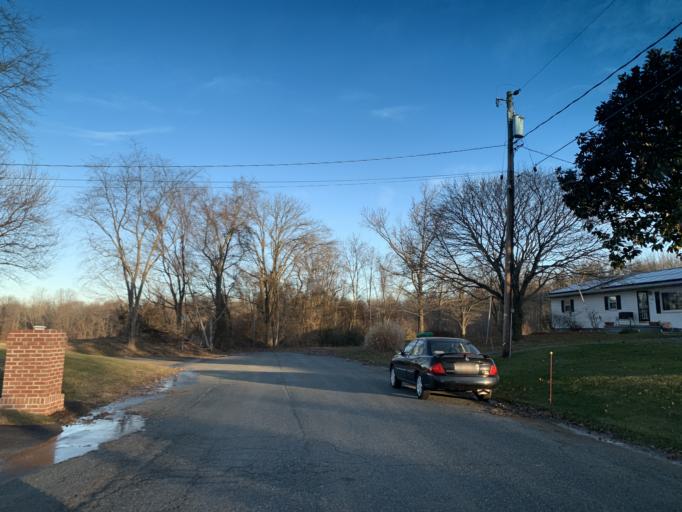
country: US
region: Maryland
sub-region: Harford County
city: Aberdeen
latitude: 39.5653
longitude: -76.2105
